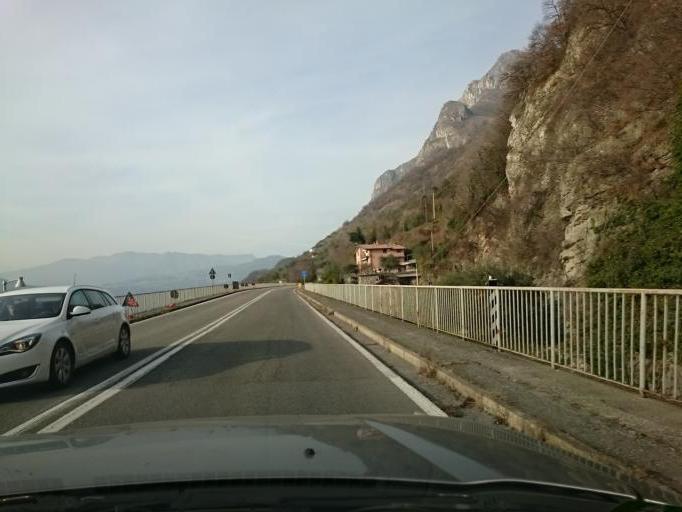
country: IT
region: Lombardy
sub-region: Provincia di Brescia
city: Marone
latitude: 45.7505
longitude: 10.0860
